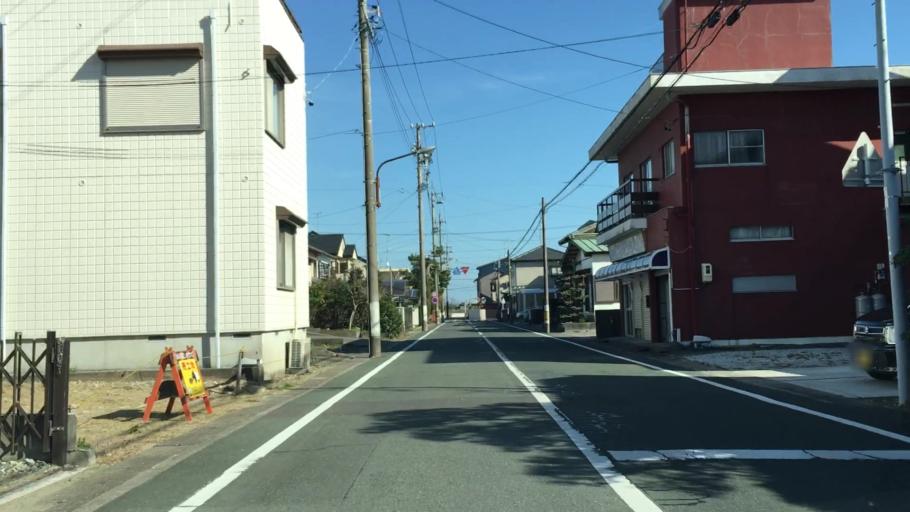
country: JP
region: Shizuoka
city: Kosai-shi
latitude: 34.6950
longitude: 137.6053
